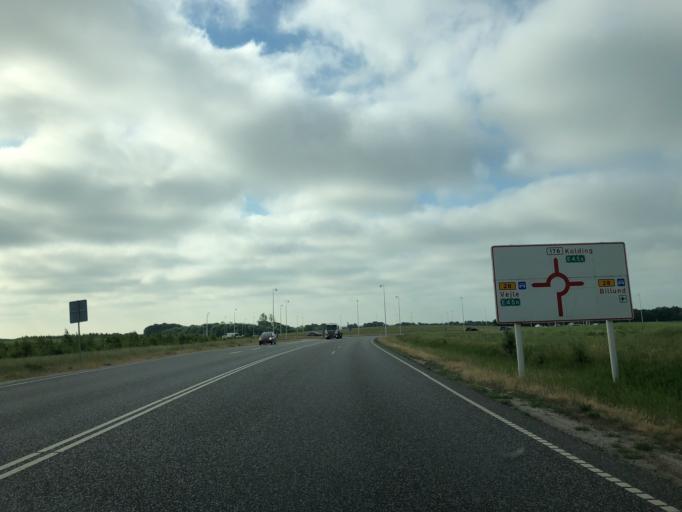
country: DK
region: South Denmark
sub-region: Vejle Kommune
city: Jelling
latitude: 55.6996
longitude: 9.3730
